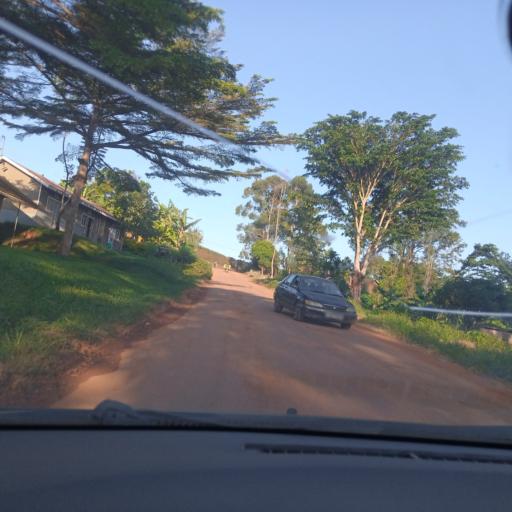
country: UG
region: Central Region
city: Masaka
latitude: -0.3359
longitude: 31.7608
